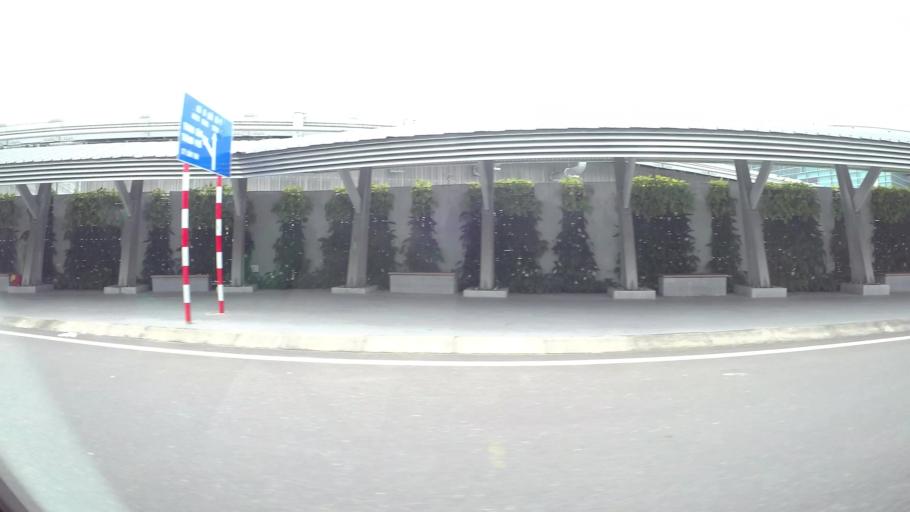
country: VN
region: Da Nang
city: Thanh Khe
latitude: 16.0549
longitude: 108.2030
